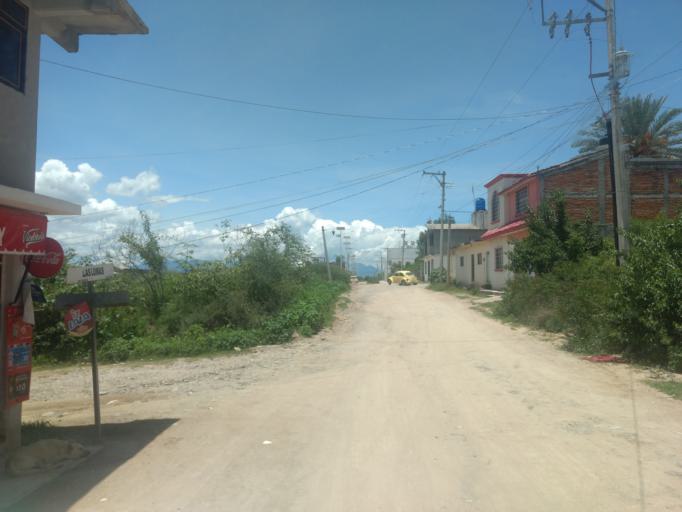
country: MX
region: Oaxaca
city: Ciudad de Huajuapam de Leon
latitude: 17.8163
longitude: -97.7941
